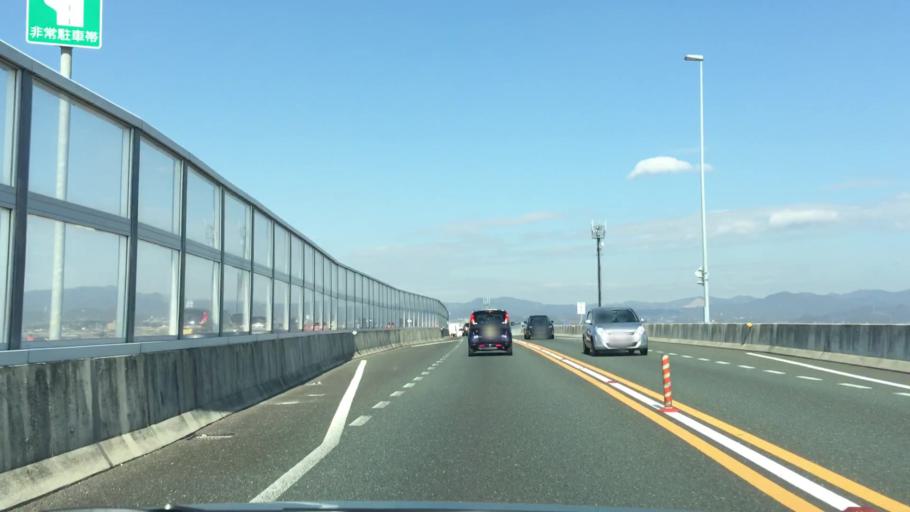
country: JP
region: Aichi
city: Kozakai-cho
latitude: 34.7850
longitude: 137.3329
